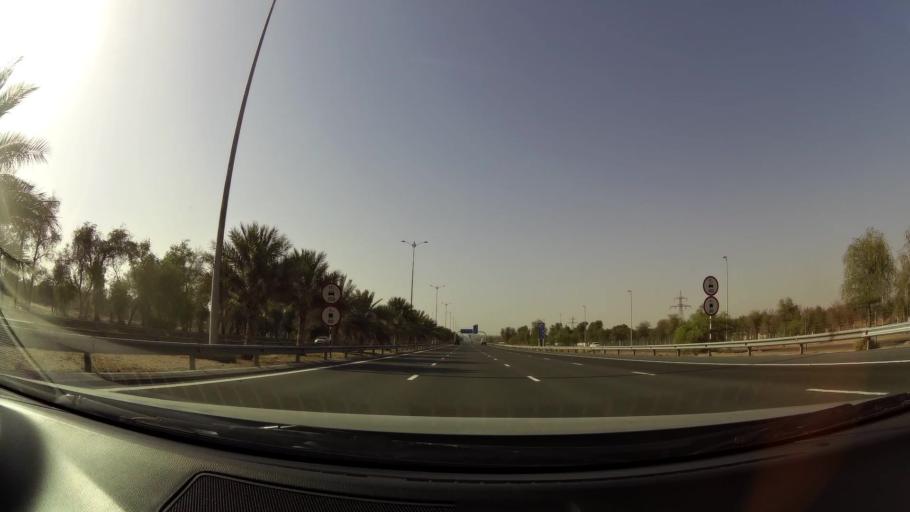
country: OM
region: Al Buraimi
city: Al Buraymi
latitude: 24.5989
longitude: 55.7337
